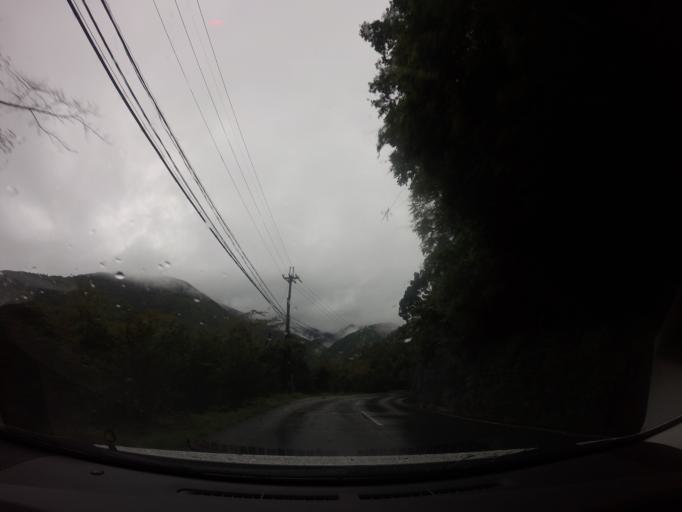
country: JP
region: Wakayama
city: Koya
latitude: 34.0623
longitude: 135.7508
